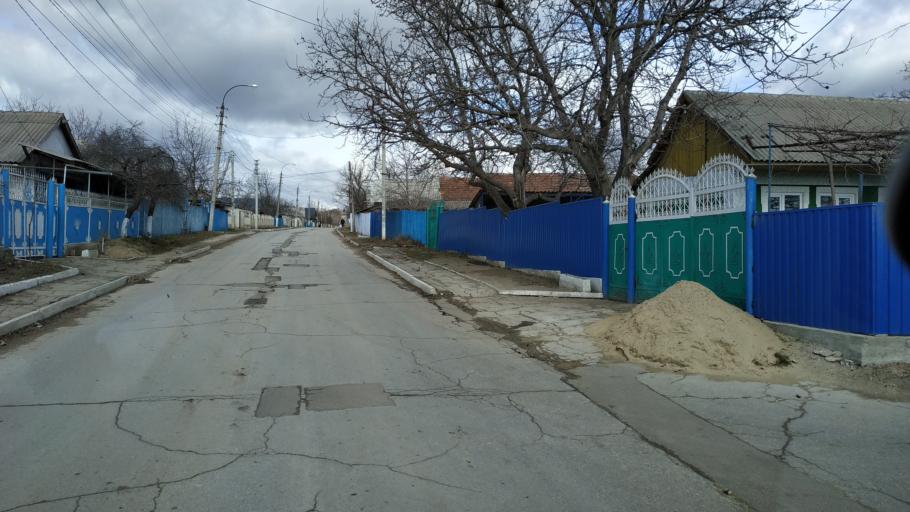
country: MD
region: Stinga Nistrului
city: Bucovat
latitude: 47.2084
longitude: 28.4958
